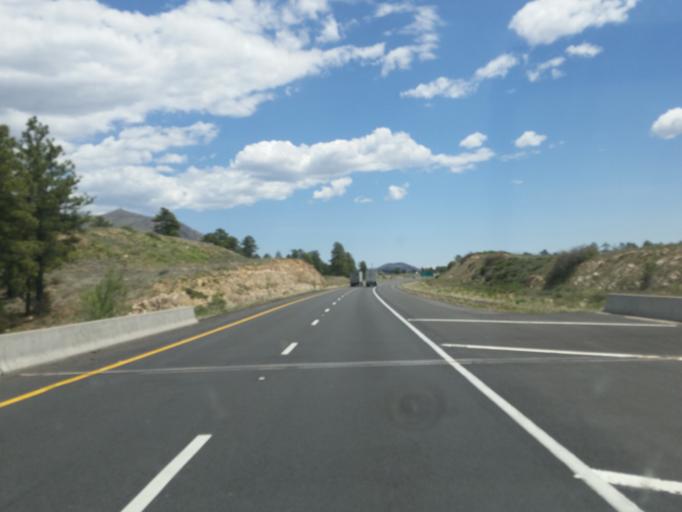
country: US
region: Arizona
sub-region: Coconino County
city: Flagstaff
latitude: 35.1845
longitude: -111.6326
